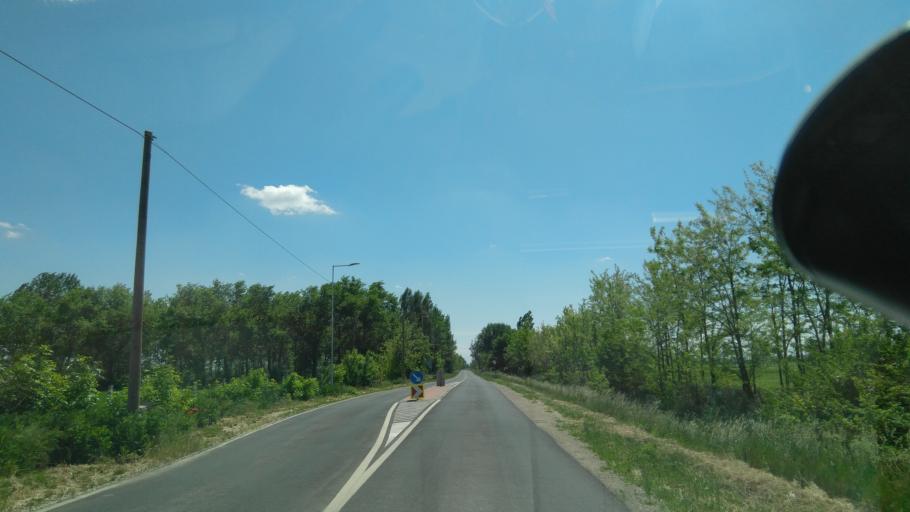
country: HU
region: Bekes
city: Kunagota
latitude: 46.4150
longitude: 21.0428
